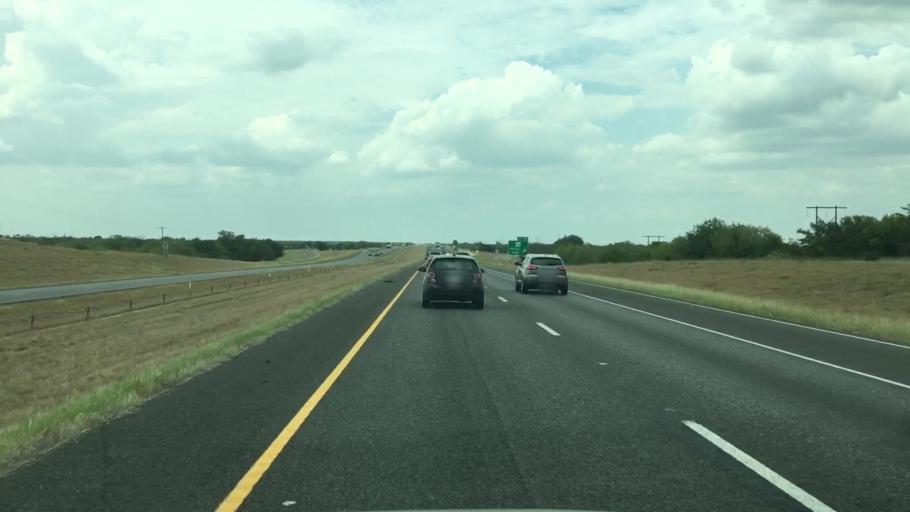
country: US
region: Texas
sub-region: Atascosa County
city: Pleasanton
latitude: 28.8373
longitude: -98.3730
